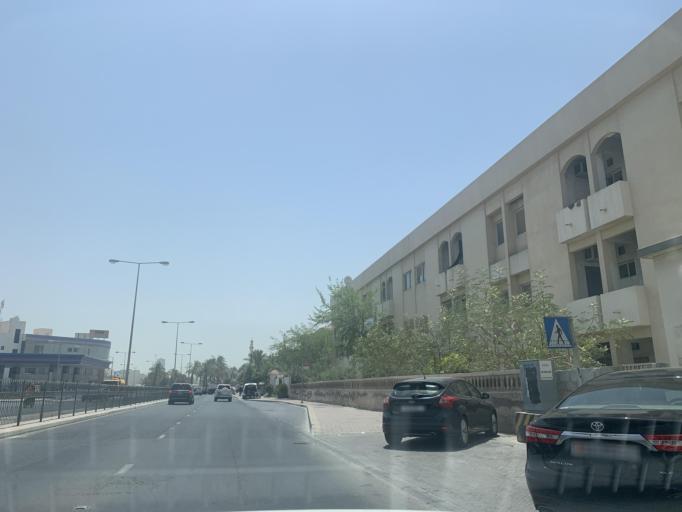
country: BH
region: Manama
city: Jidd Hafs
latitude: 26.2197
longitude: 50.5337
